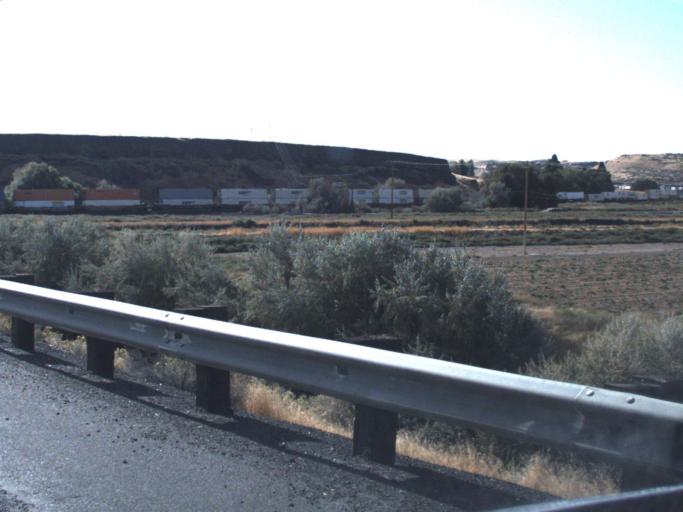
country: US
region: Washington
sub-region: Franklin County
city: Basin City
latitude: 46.5881
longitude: -119.0043
